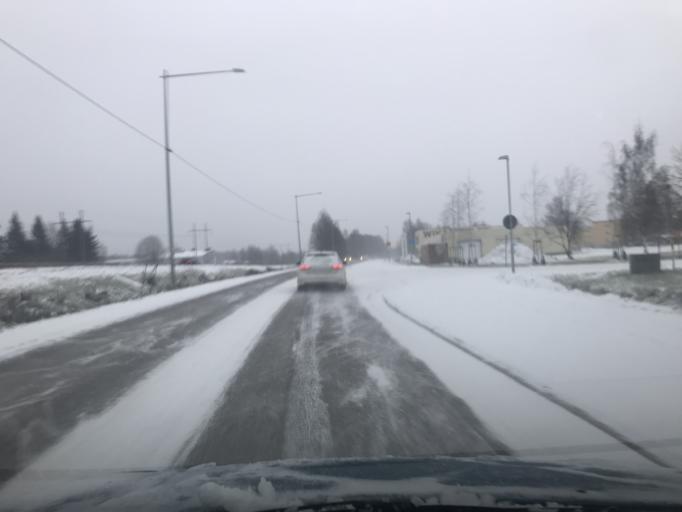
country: SE
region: Norrbotten
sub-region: Lulea Kommun
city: Gammelstad
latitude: 65.6414
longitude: 22.0164
